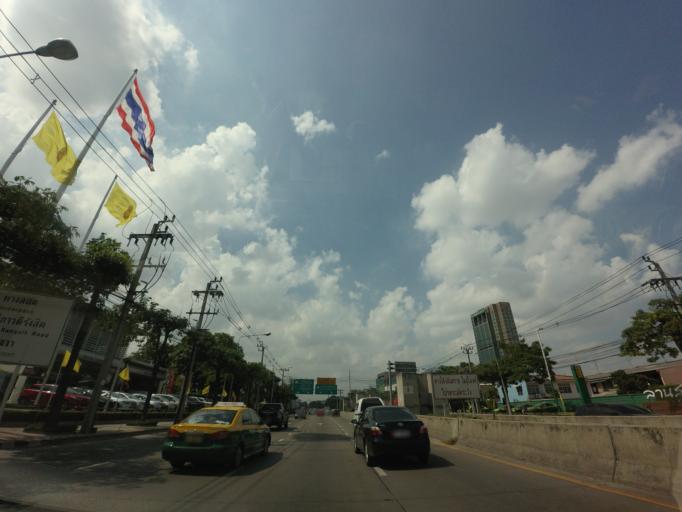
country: TH
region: Bangkok
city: Chatuchak
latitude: 13.8405
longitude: 100.5810
